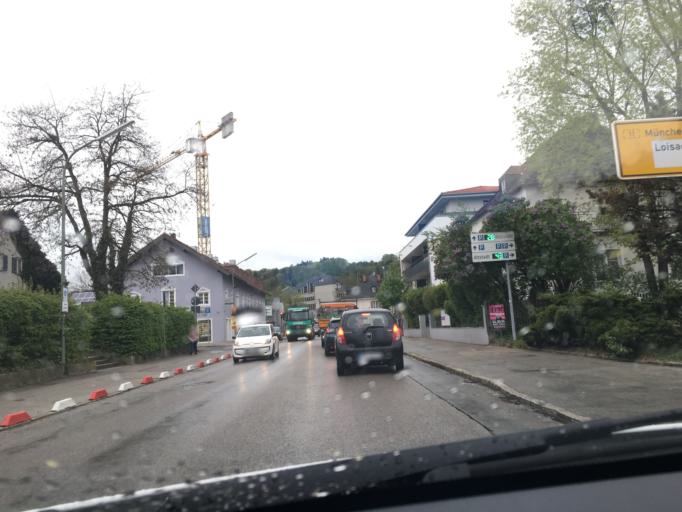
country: DE
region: Bavaria
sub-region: Upper Bavaria
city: Wolfratshausen
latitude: 47.9133
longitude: 11.4262
